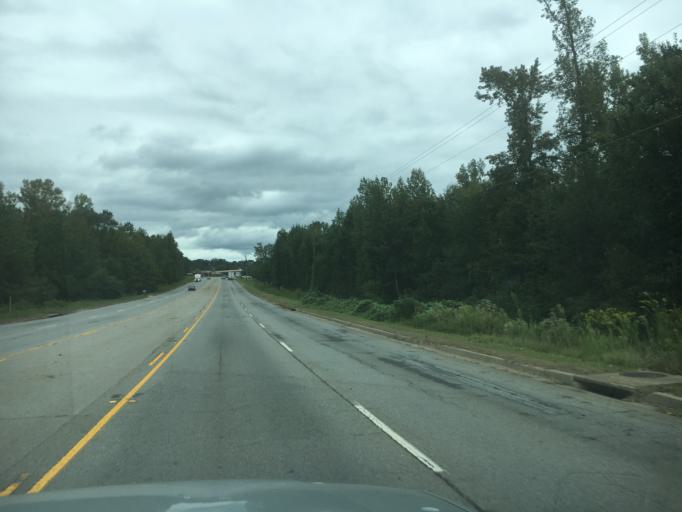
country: US
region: South Carolina
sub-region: Anderson County
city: Honea Path
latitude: 34.5084
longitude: -82.3010
